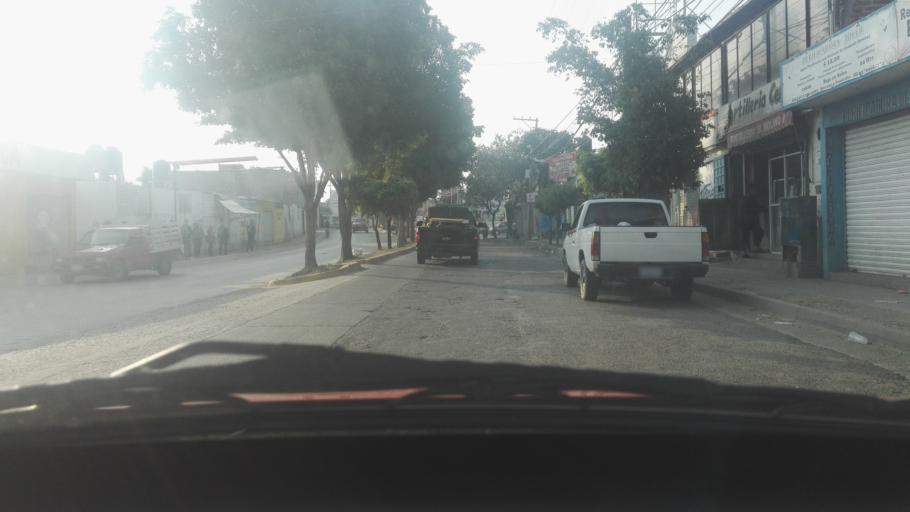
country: MX
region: Guanajuato
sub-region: Leon
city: Fraccionamiento Paraiso Real
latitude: 21.0978
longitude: -101.6052
